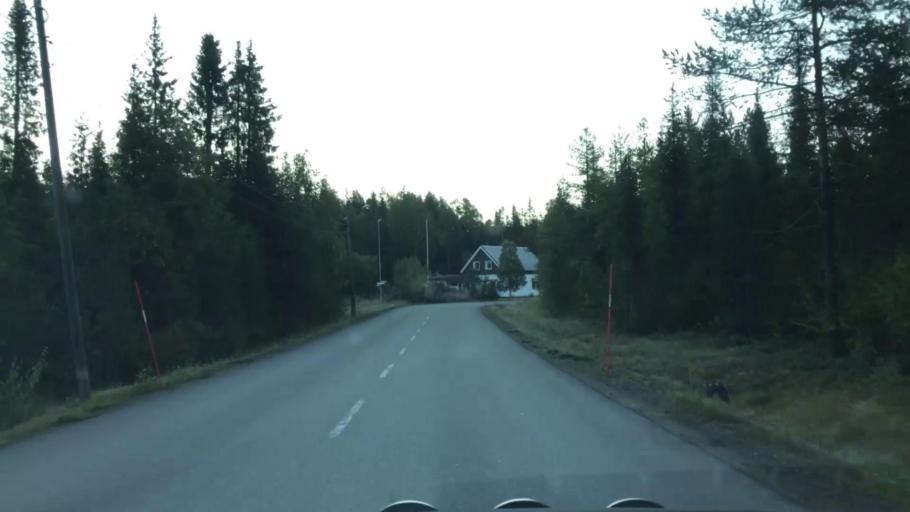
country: SE
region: Norrbotten
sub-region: Gallivare Kommun
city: Malmberget
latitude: 67.6515
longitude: 21.0399
